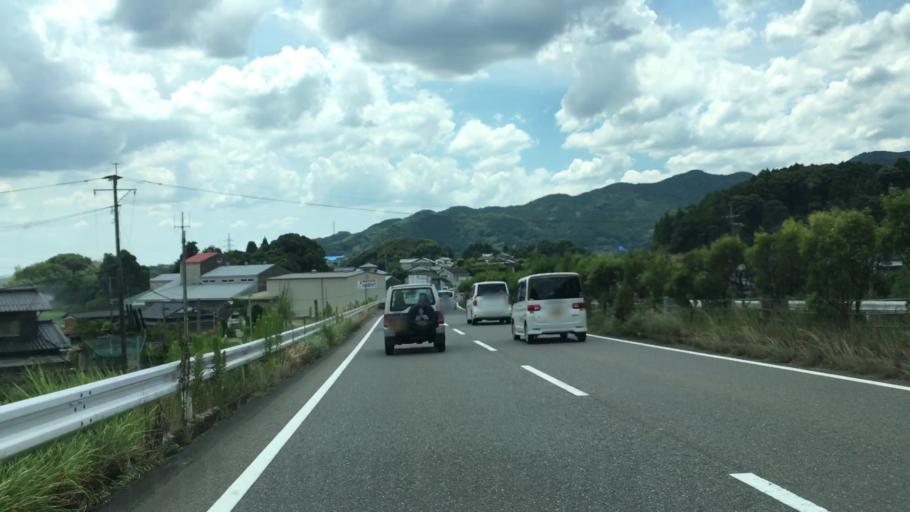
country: JP
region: Saga Prefecture
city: Tosu
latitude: 33.4273
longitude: 130.5179
